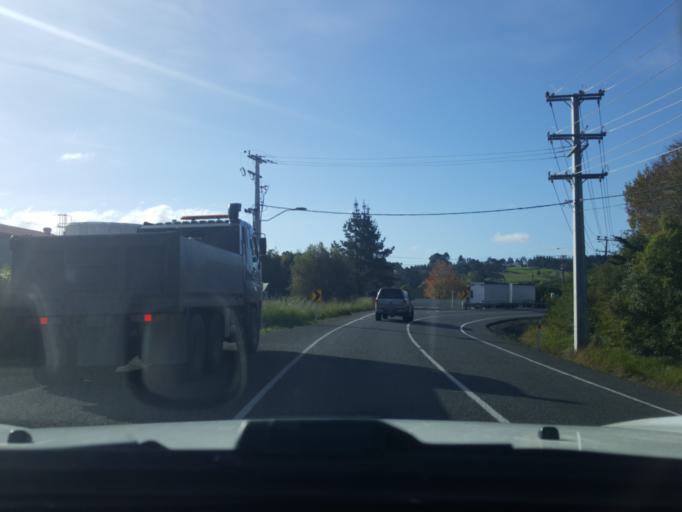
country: NZ
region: Auckland
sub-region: Auckland
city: Muriwai Beach
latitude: -36.7635
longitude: 174.5769
